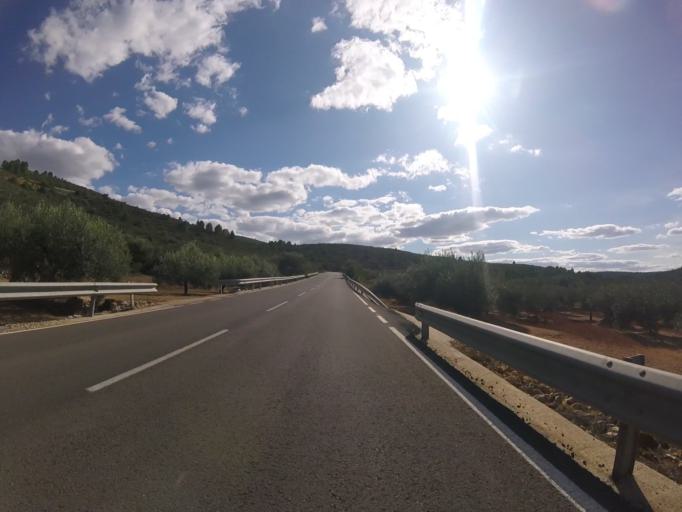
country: ES
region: Valencia
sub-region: Provincia de Castello
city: Cuevas de Vinroma
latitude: 40.2990
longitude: 0.1678
